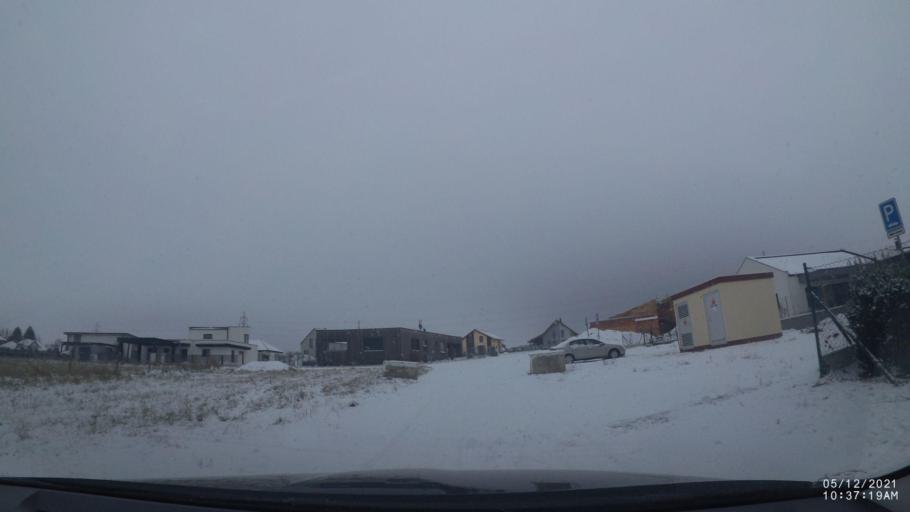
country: CZ
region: Kralovehradecky
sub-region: Okres Rychnov nad Kneznou
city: Rychnov nad Kneznou
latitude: 50.1656
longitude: 16.2906
